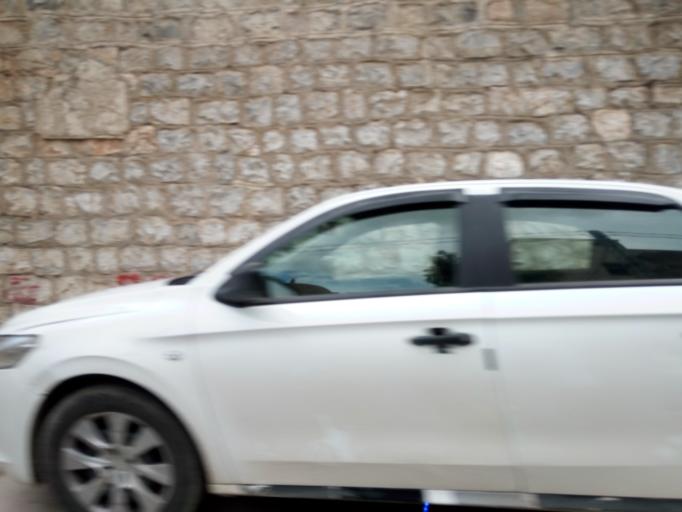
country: DZ
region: Constantine
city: Constantine
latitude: 36.3597
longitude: 6.6076
